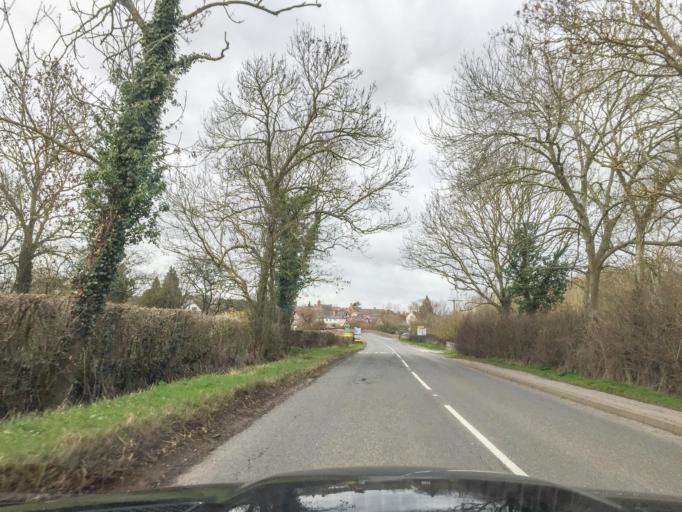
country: GB
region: England
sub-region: Warwickshire
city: Shipston on Stour
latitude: 52.0610
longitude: -1.6198
